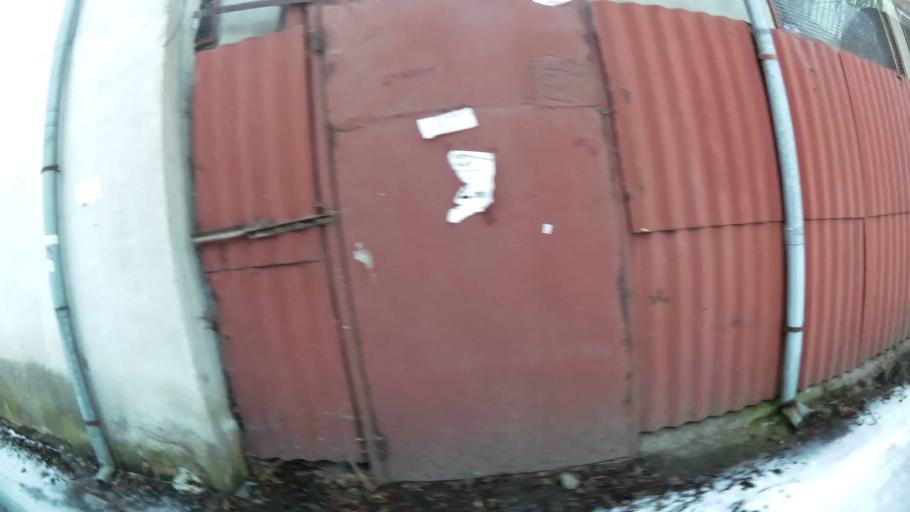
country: BG
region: Sofia-Capital
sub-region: Stolichna Obshtina
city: Sofia
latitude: 42.7040
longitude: 23.3449
